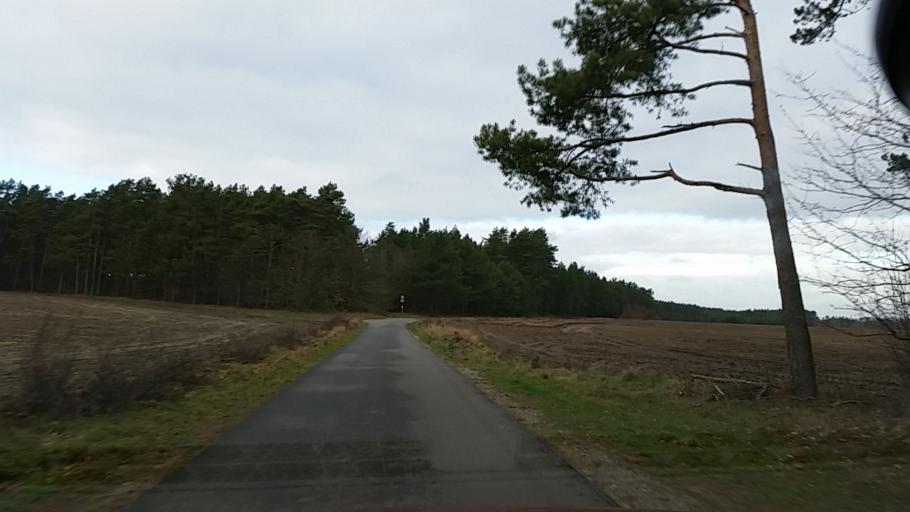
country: DE
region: Lower Saxony
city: Wieren
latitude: 52.8556
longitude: 10.6599
